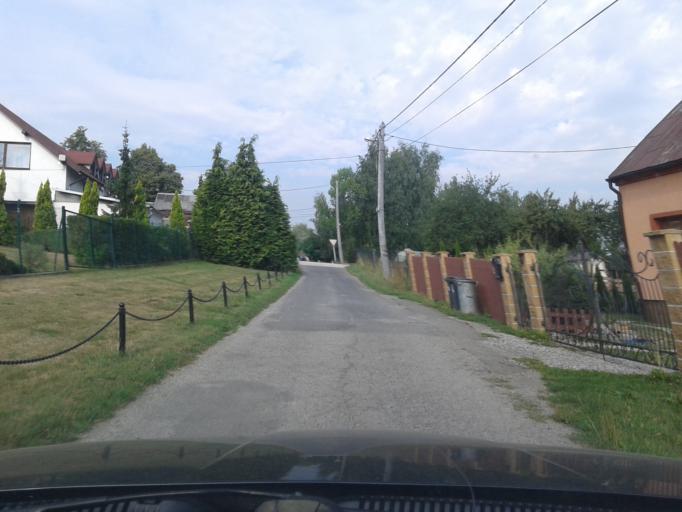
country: CZ
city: Dolni Lutyne
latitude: 49.8847
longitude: 18.4357
